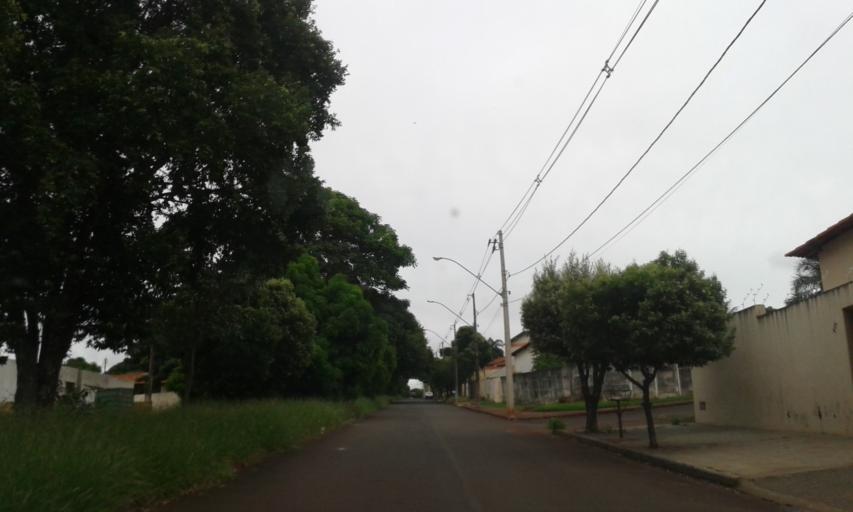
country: BR
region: Minas Gerais
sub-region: Ituiutaba
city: Ituiutaba
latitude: -18.9720
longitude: -49.4513
